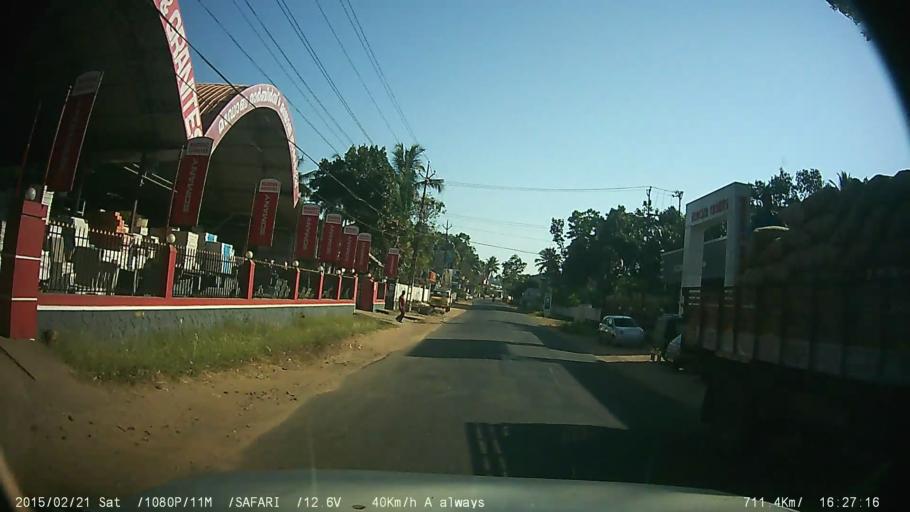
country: IN
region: Kerala
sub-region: Kottayam
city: Kottayam
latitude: 9.5391
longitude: 76.5135
